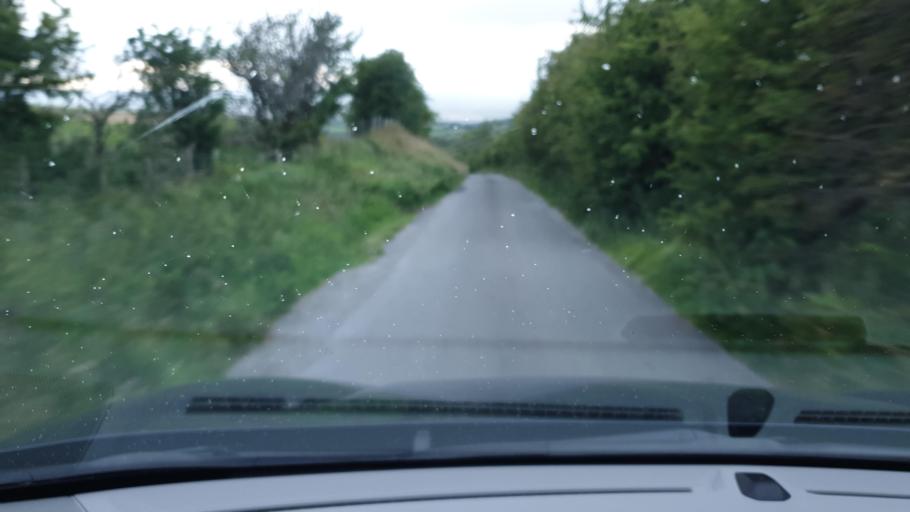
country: IE
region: Leinster
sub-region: Wicklow
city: Blessington
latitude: 53.2230
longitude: -6.4985
